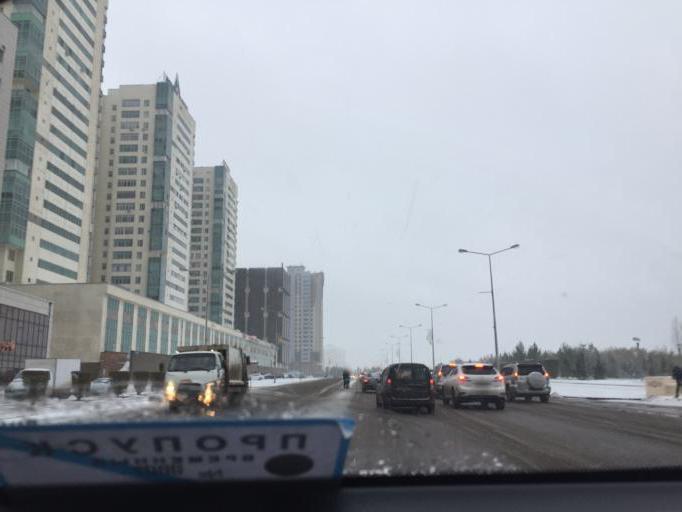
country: KZ
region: Astana Qalasy
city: Astana
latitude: 51.1330
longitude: 71.4595
